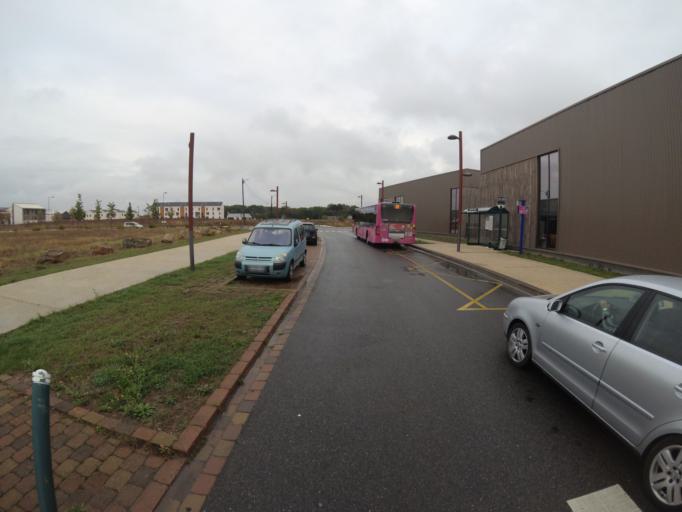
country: FR
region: Ile-de-France
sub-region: Departement de Seine-et-Marne
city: Chanteloup-en-Brie
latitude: 48.8555
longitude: 2.7461
